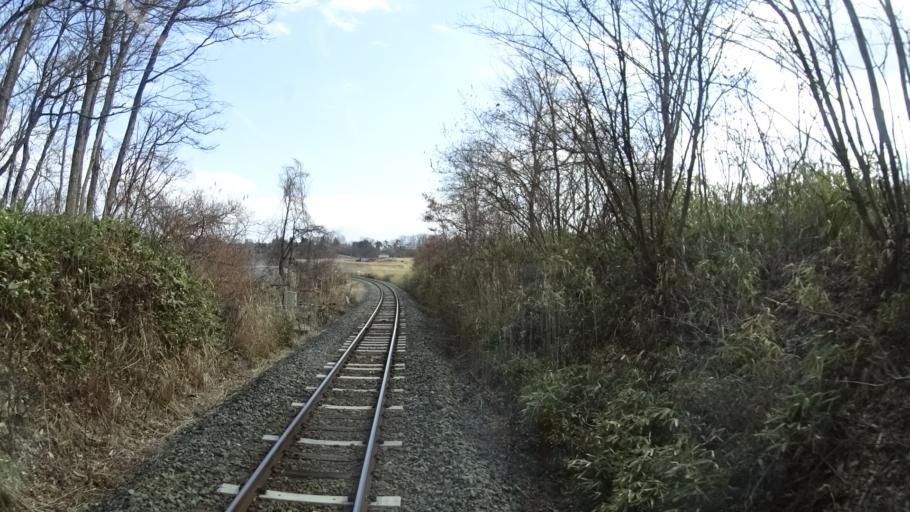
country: JP
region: Iwate
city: Hanamaki
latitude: 39.3953
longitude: 141.2122
